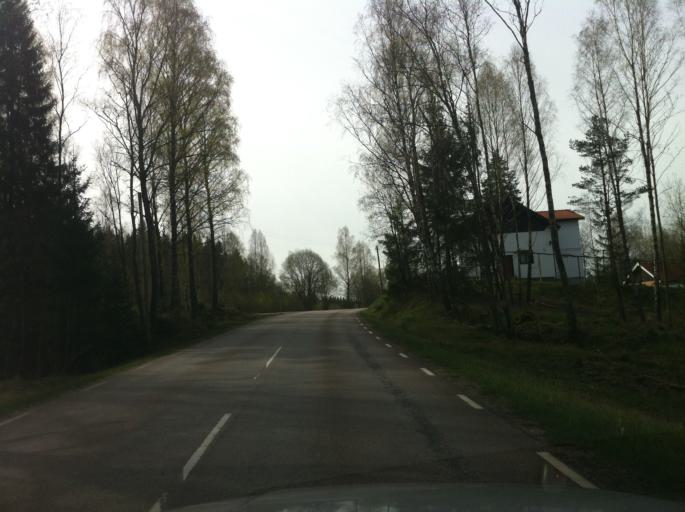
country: SE
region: Vaestra Goetaland
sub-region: Bollebygds Kommun
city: Bollebygd
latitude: 57.7203
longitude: 12.5853
